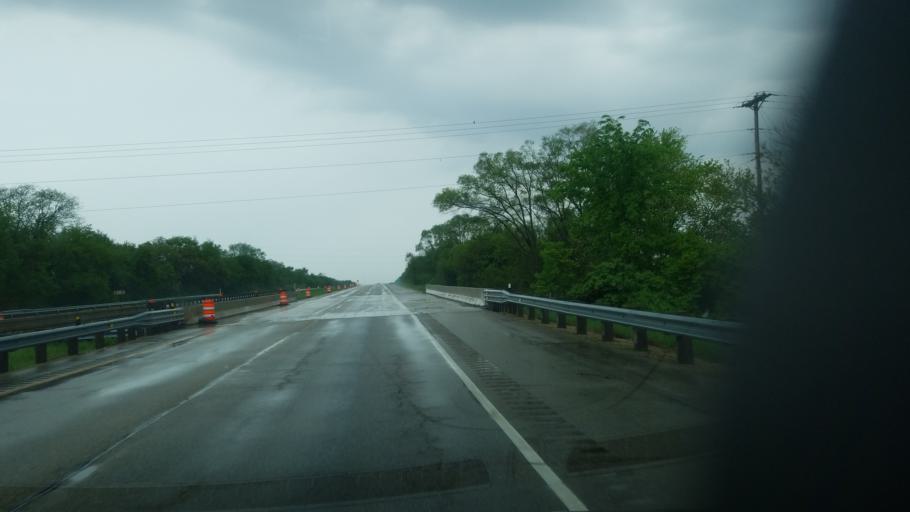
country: US
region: Wisconsin
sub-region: Dane County
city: Oregon
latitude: 42.9863
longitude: -89.3862
